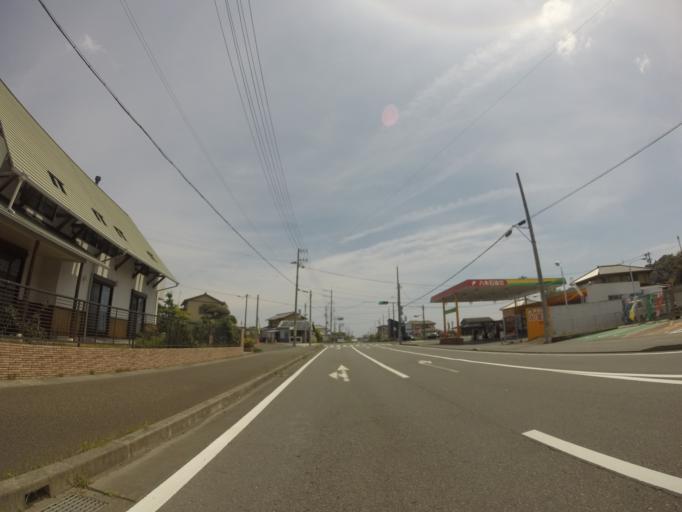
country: JP
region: Shizuoka
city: Fujieda
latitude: 34.8932
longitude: 138.2506
